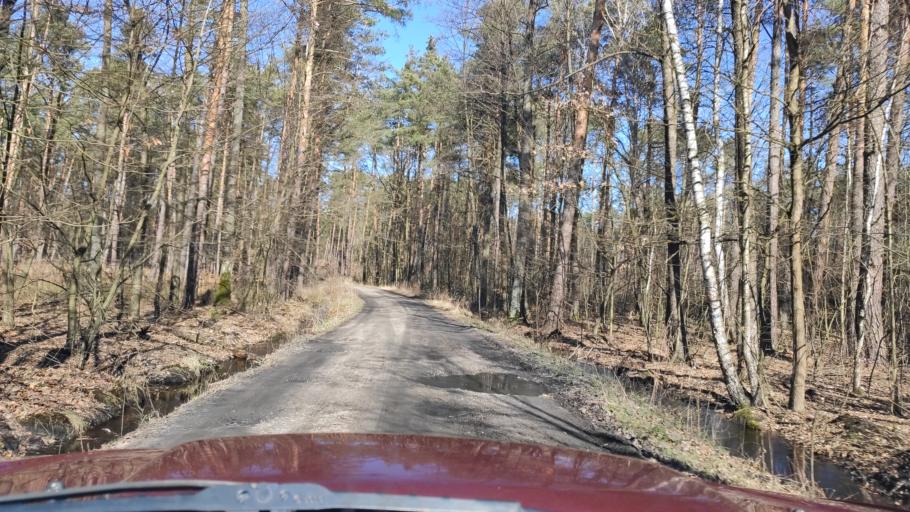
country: PL
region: Masovian Voivodeship
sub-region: Powiat kozienicki
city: Garbatka-Letnisko
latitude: 51.4430
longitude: 21.5364
